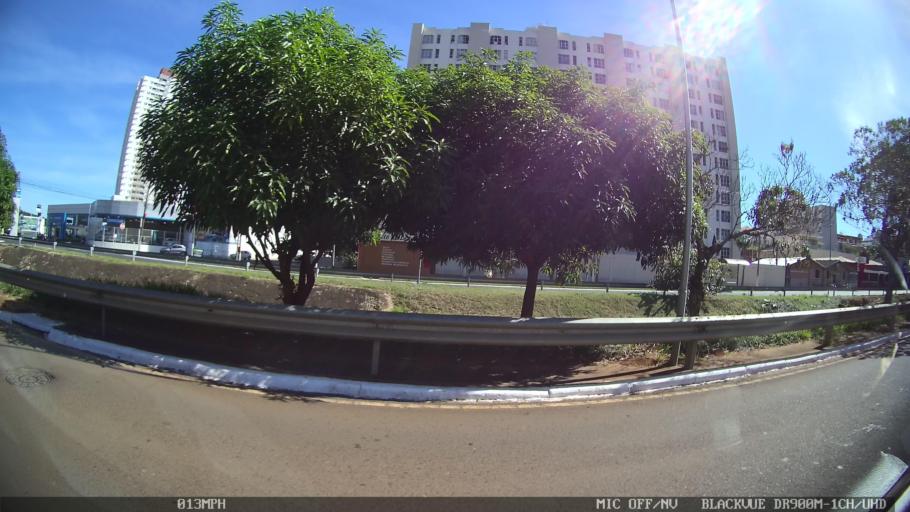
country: BR
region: Sao Paulo
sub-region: Franca
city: Franca
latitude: -20.5505
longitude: -47.4035
